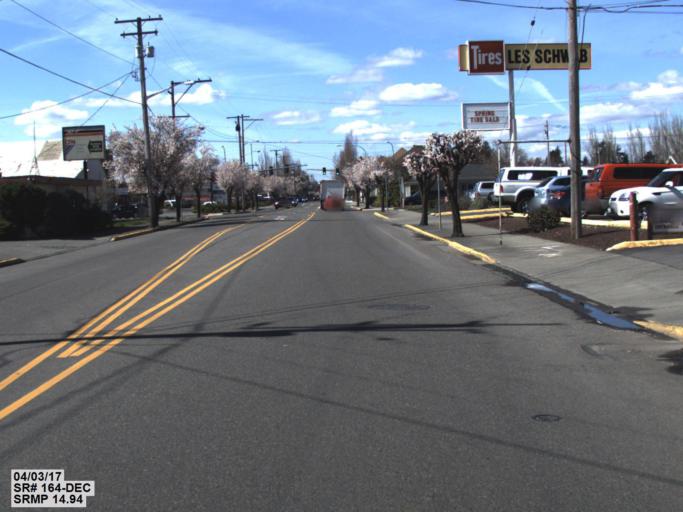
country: US
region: Washington
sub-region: King County
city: Enumclaw
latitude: 47.2009
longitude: -121.9843
